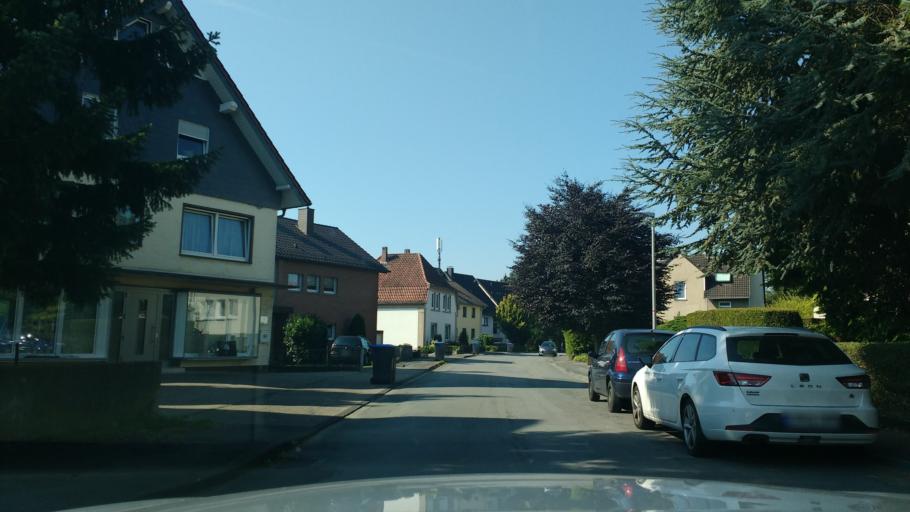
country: DE
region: North Rhine-Westphalia
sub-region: Regierungsbezirk Detmold
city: Lemgo
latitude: 52.0272
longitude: 8.9244
